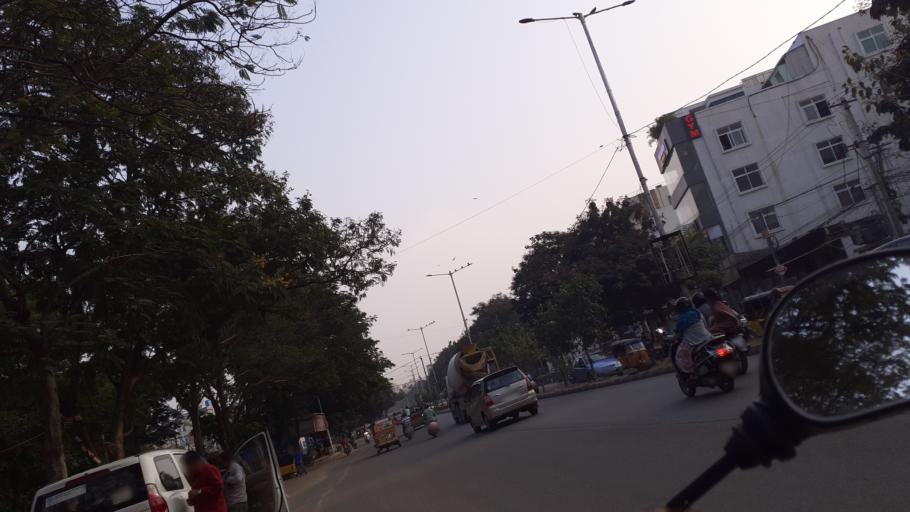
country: IN
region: Telangana
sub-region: Rangareddi
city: Kukatpalli
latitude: 17.4734
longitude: 78.3643
